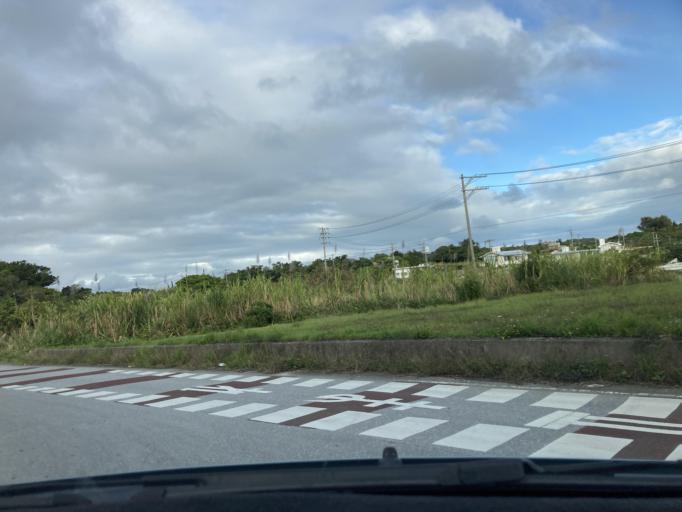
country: JP
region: Okinawa
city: Itoman
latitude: 26.1147
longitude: 127.6808
